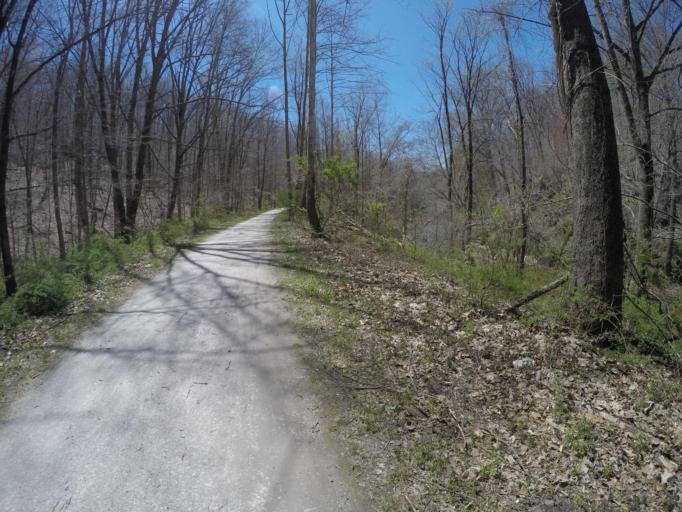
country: US
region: Maryland
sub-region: Baltimore County
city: Hunt Valley
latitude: 39.5619
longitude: -76.6320
